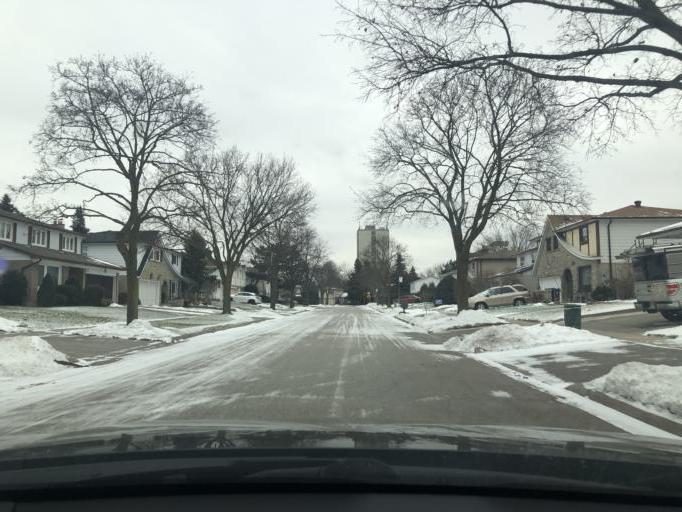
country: CA
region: Ontario
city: Scarborough
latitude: 43.7843
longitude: -79.3056
